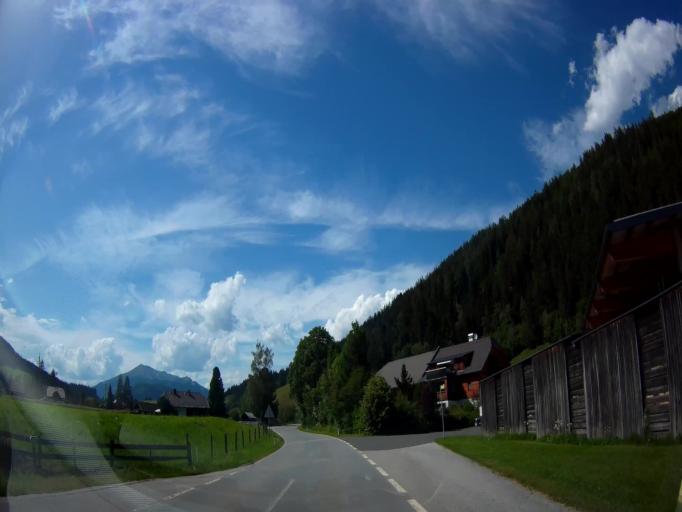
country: AT
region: Salzburg
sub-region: Politischer Bezirk Tamsweg
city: Thomatal
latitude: 47.0757
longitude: 13.7407
